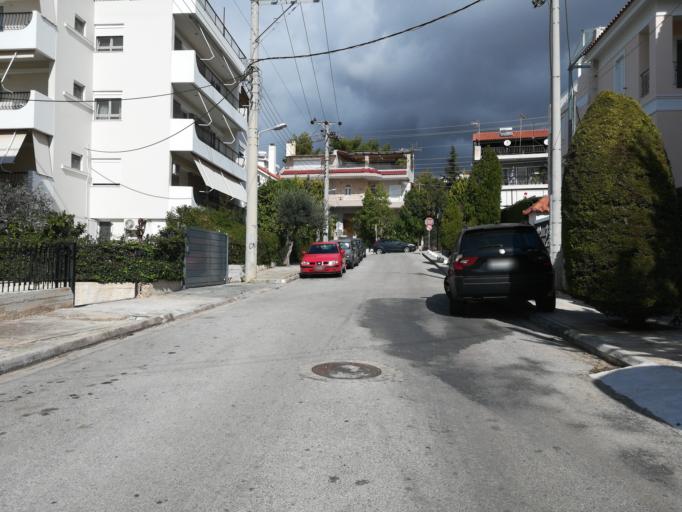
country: GR
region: Attica
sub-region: Nomarchia Anatolikis Attikis
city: Voula
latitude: 37.8461
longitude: 23.7750
